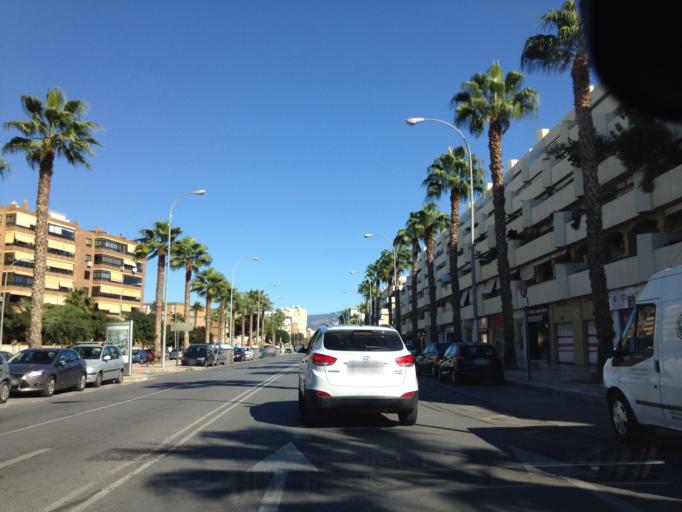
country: ES
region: Andalusia
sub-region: Provincia de Malaga
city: Malaga
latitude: 36.6872
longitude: -4.4526
